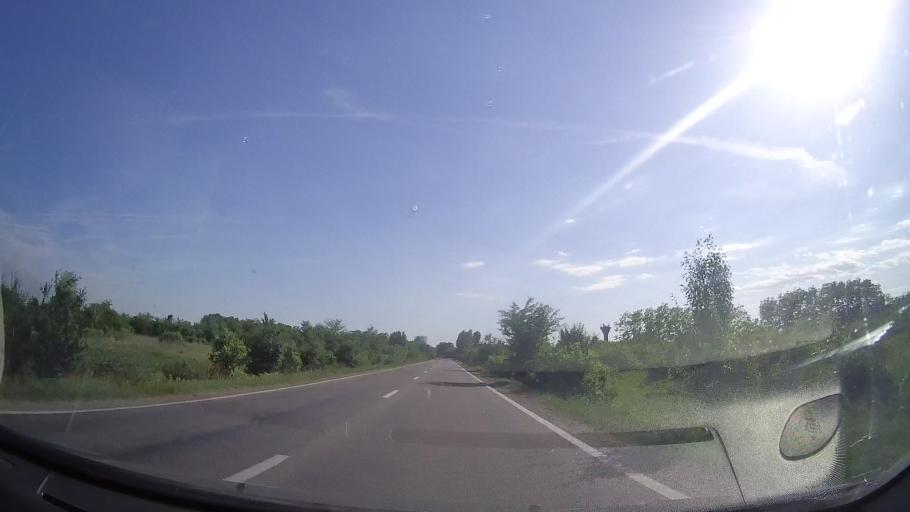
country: RO
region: Prahova
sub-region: Comuna Barcanesti
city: Barcanesti
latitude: 44.8913
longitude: 26.0491
